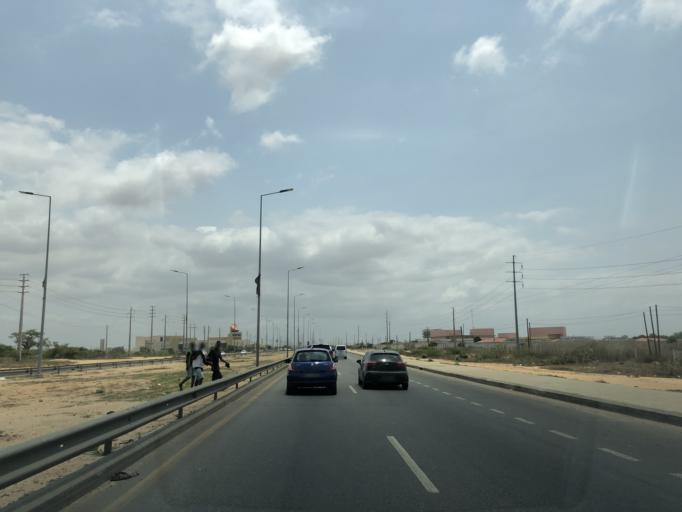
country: AO
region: Luanda
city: Luanda
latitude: -8.9550
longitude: 13.2581
